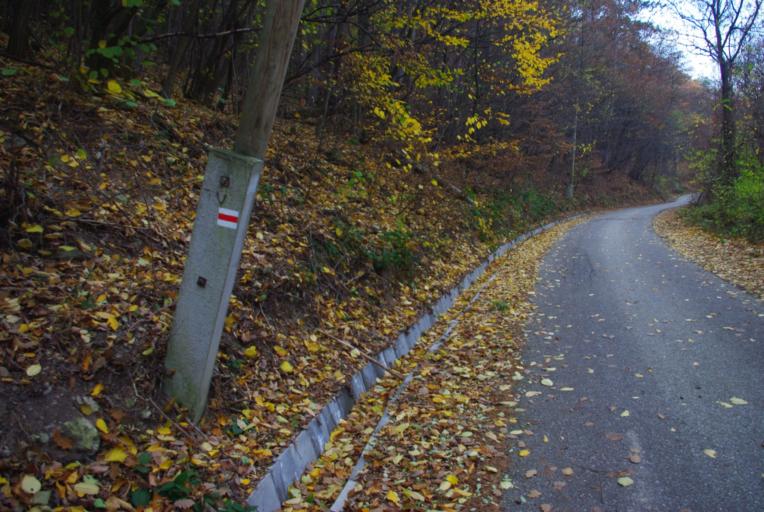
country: HU
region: Borsod-Abauj-Zemplen
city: Satoraljaujhely
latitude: 48.3959
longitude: 21.6357
